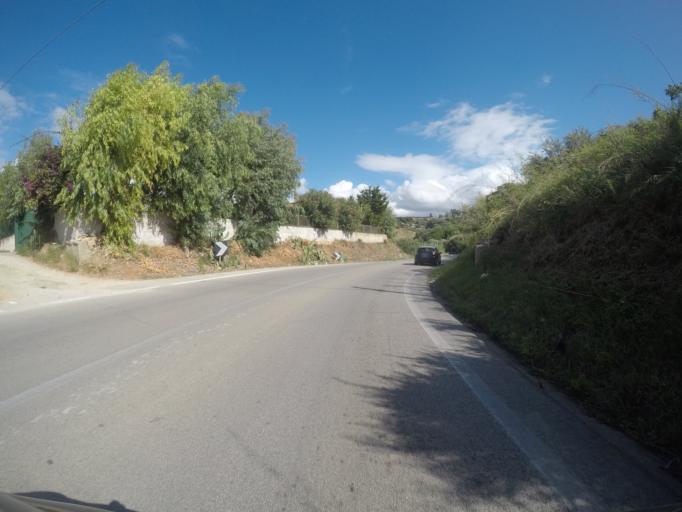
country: IT
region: Sicily
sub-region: Palermo
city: Trappeto
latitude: 38.0736
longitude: 13.0701
